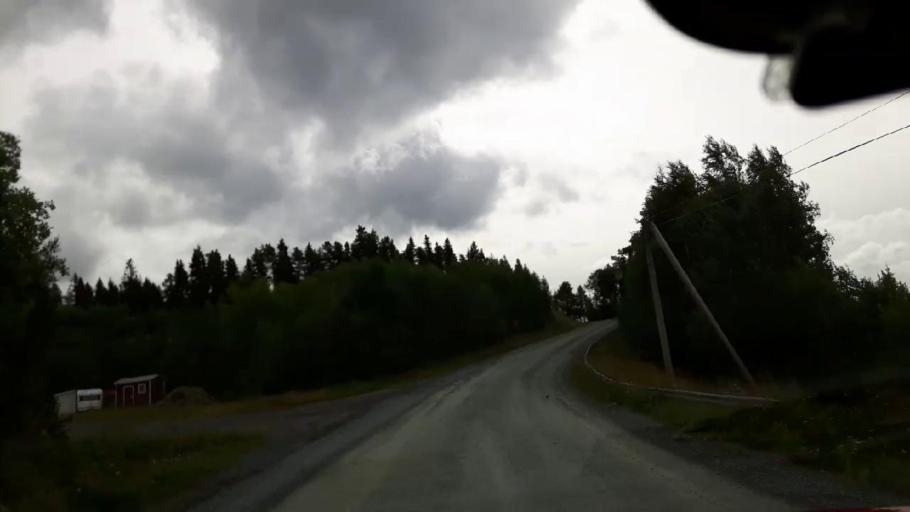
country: SE
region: Jaemtland
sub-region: Krokoms Kommun
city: Krokom
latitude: 63.5708
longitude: 14.2405
